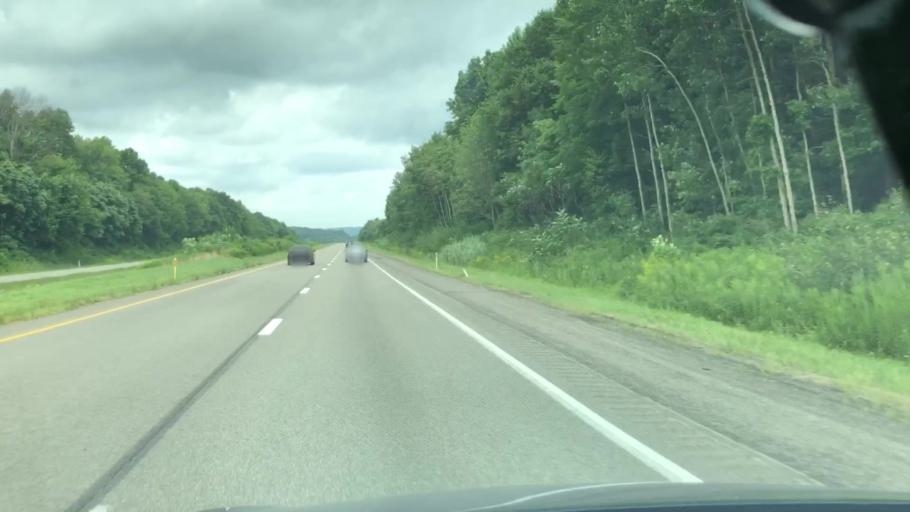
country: US
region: Pennsylvania
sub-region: Crawford County
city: Meadville
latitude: 41.5748
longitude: -80.1807
